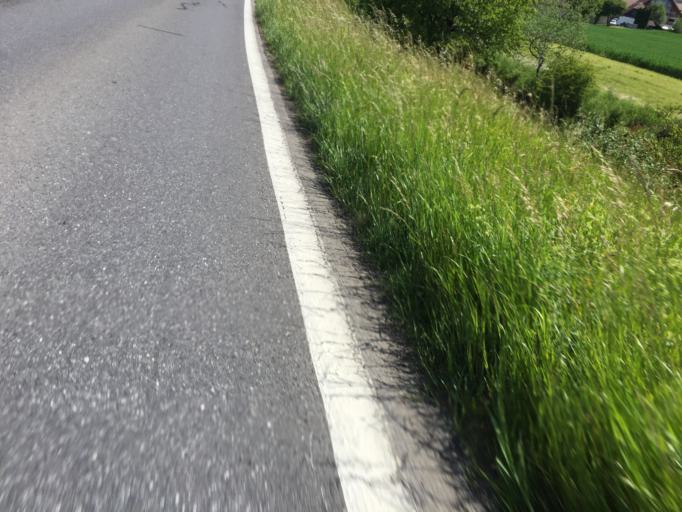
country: CH
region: Bern
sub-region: Bern-Mittelland District
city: Zaziwil
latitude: 46.8956
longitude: 7.6579
